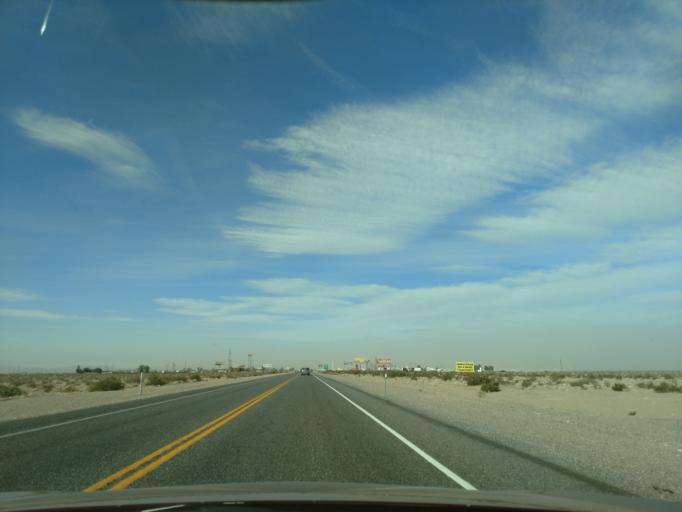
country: US
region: Nevada
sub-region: Nye County
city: Beatty
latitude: 36.6410
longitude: -116.3891
